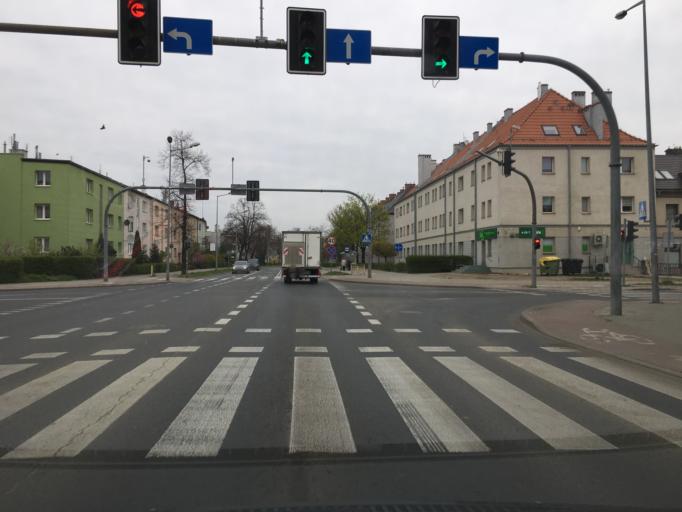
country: PL
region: Lower Silesian Voivodeship
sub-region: Legnica
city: Legnica
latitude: 51.1951
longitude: 16.1775
